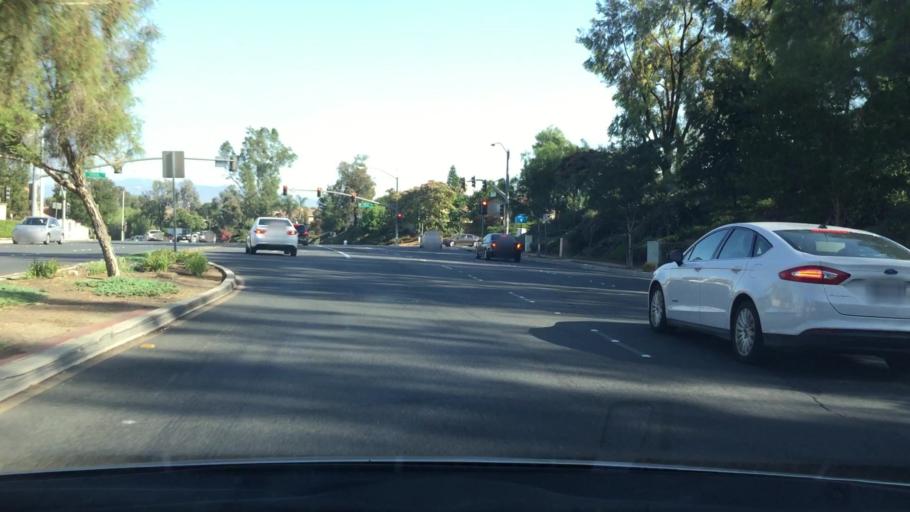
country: US
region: California
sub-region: San Bernardino County
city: Chino Hills
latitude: 34.0111
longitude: -117.7433
